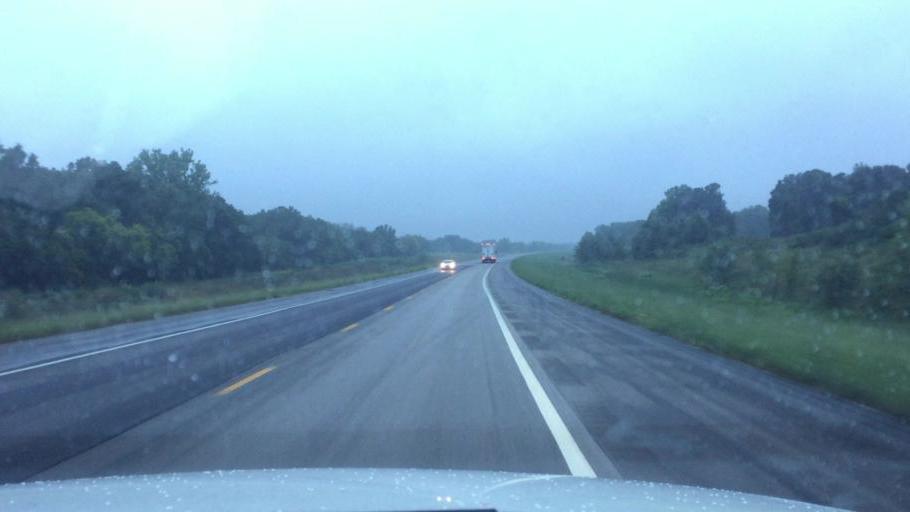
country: US
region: Kansas
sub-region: Montgomery County
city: Cherryvale
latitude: 37.4462
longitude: -95.4839
